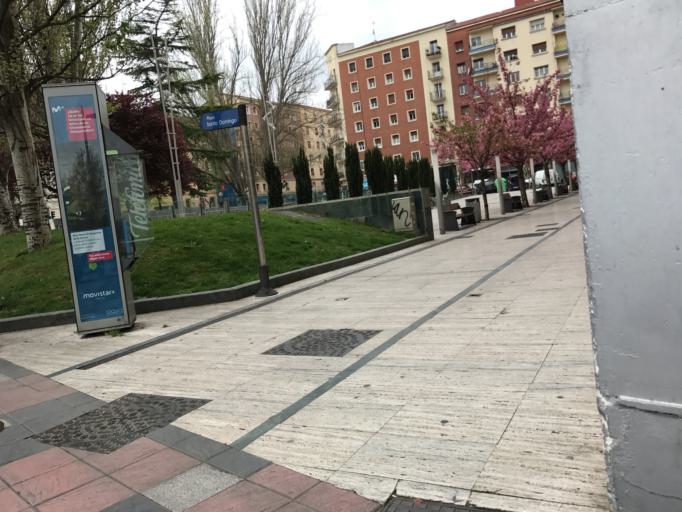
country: ES
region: Basque Country
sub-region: Provincia de Alava
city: Gasteiz / Vitoria
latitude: 42.8536
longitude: -2.6733
